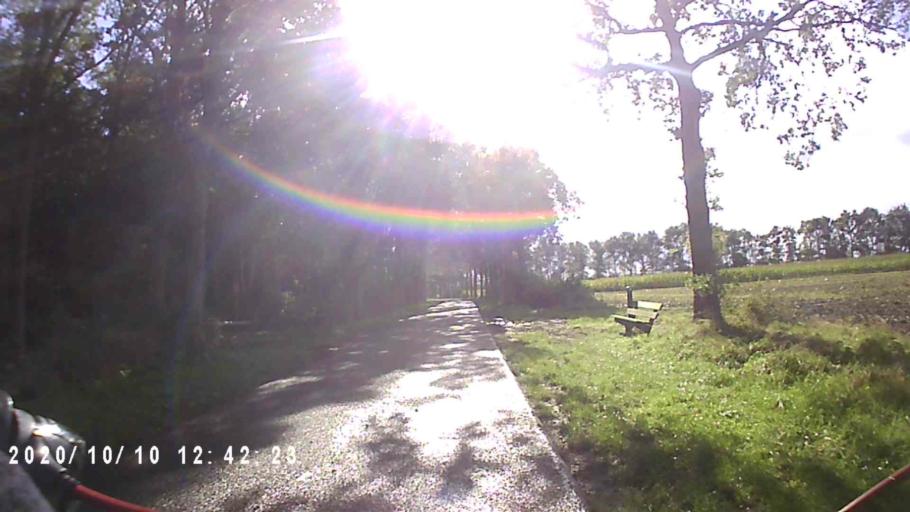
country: NL
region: Friesland
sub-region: Gemeente Weststellingwerf
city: Noordwolde
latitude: 52.9354
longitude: 6.2190
